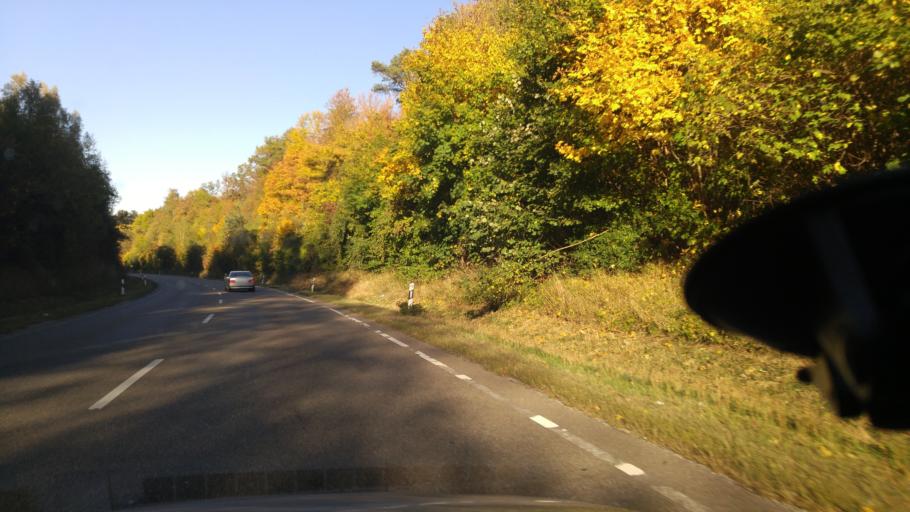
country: DE
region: Baden-Wuerttemberg
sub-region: Regierungsbezirk Stuttgart
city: Korntal
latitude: 48.8080
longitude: 9.1276
